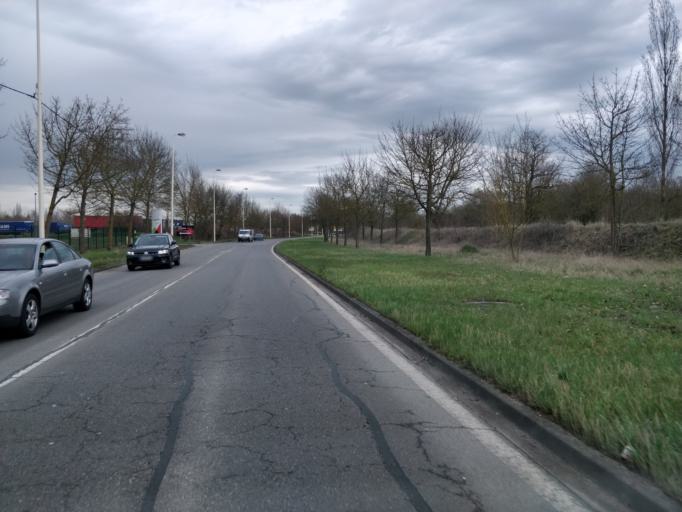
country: FR
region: Lorraine
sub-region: Departement de la Moselle
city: Terville
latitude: 49.3336
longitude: 6.1547
